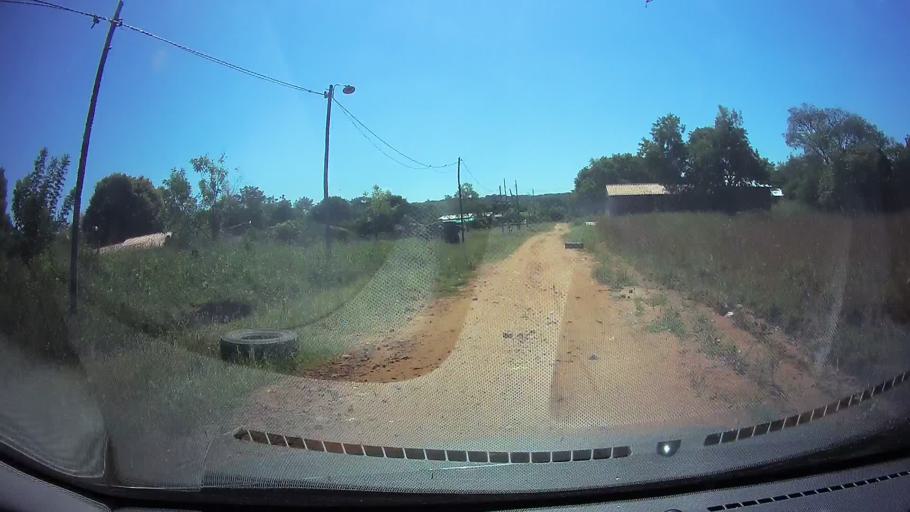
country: PY
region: Central
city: Limpio
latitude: -25.2383
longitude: -57.4511
